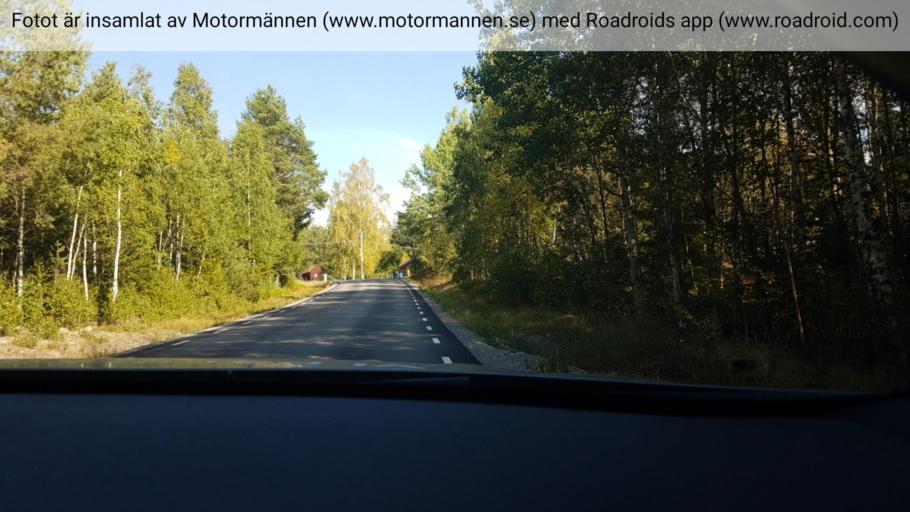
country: SE
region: Vaestra Goetaland
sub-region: Gotene Kommun
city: Goetene
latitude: 58.6210
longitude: 13.5804
